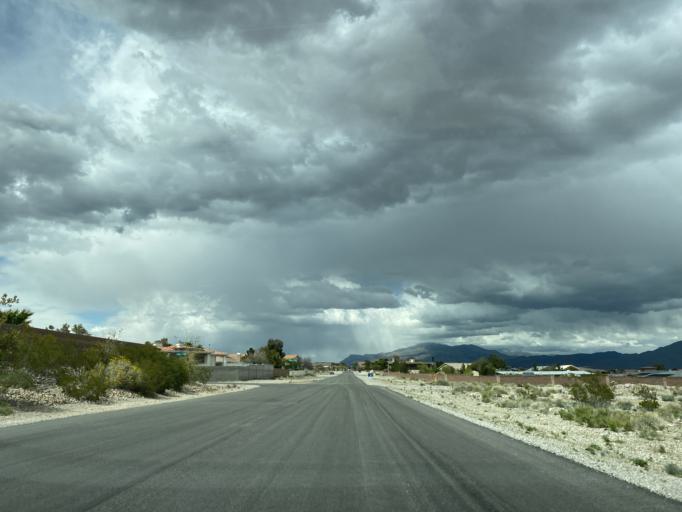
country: US
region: Nevada
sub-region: Clark County
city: Summerlin South
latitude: 36.2719
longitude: -115.3150
